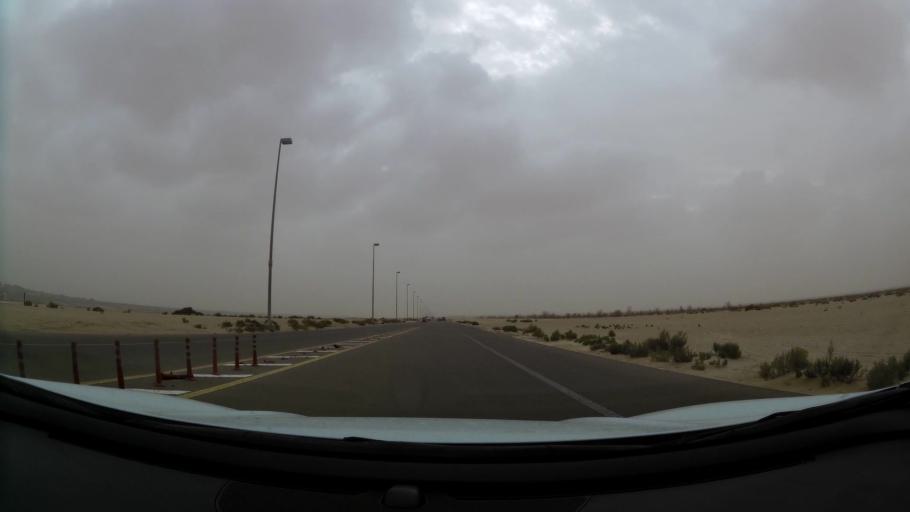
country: AE
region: Abu Dhabi
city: Abu Dhabi
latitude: 24.4612
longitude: 54.6927
